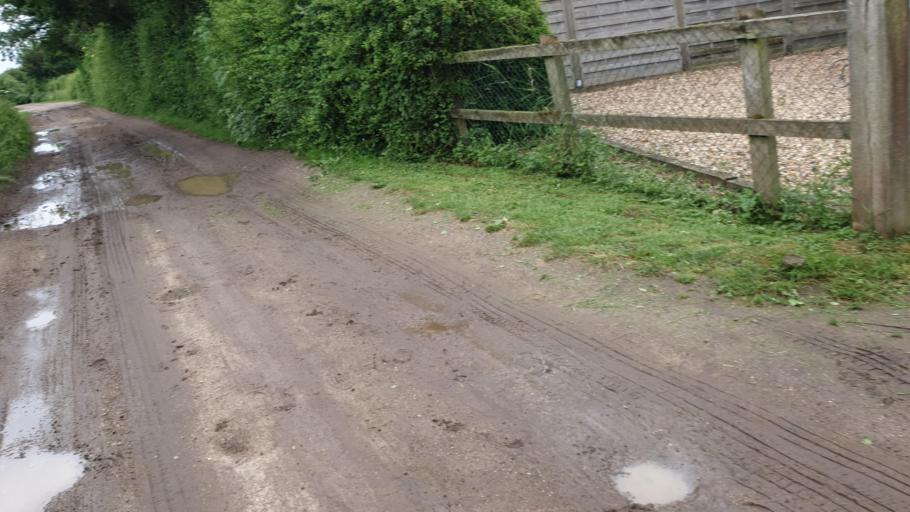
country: GB
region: England
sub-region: Essex
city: Great Bentley
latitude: 51.8803
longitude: 1.0589
